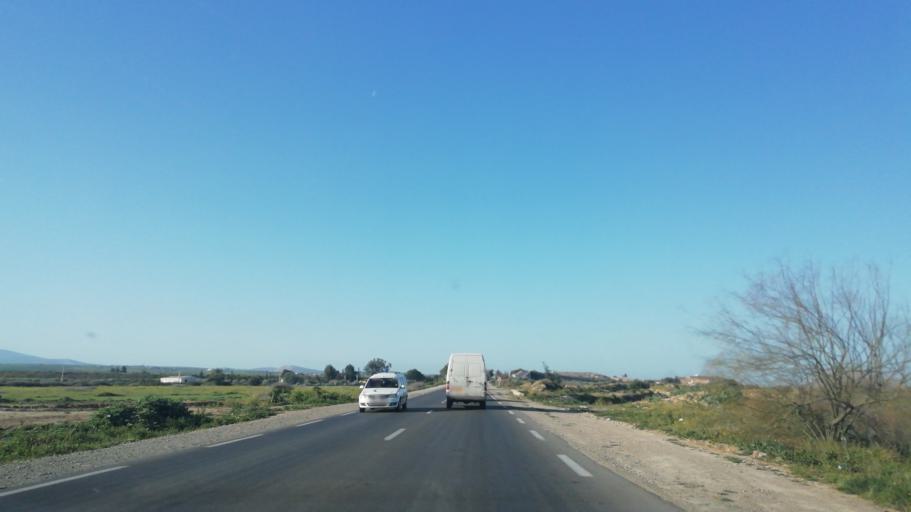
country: DZ
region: Mascara
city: Mascara
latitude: 35.6543
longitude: 0.1891
